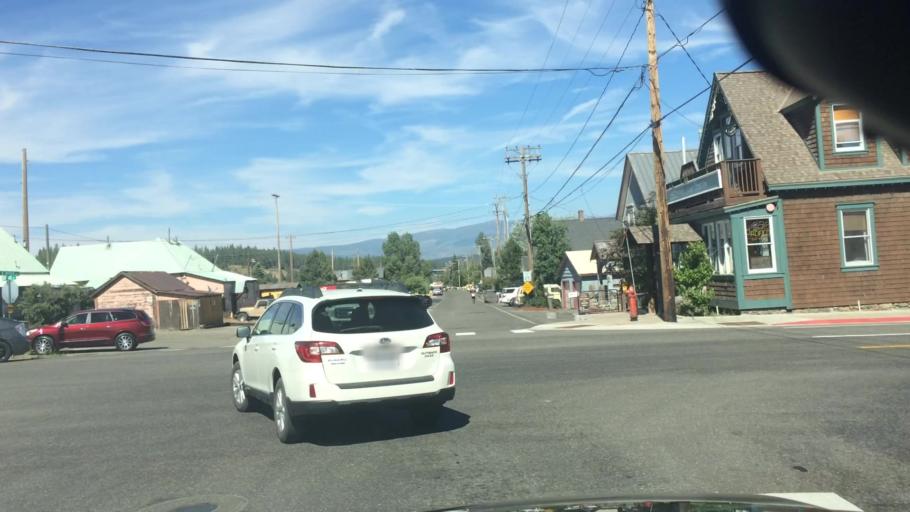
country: US
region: California
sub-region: Nevada County
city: Truckee
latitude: 39.3272
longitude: -120.1839
